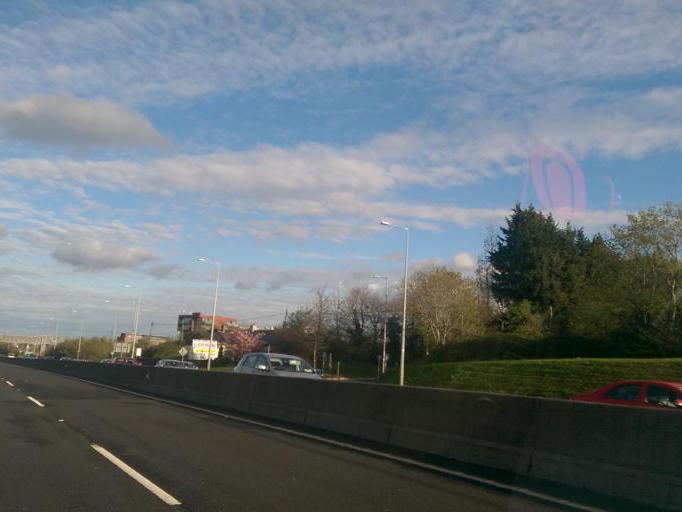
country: IE
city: Palmerstown
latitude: 53.3574
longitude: -6.4045
